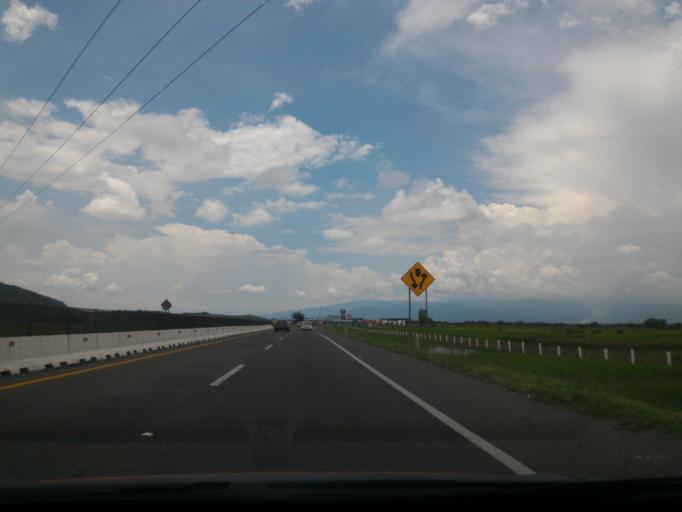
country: MX
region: Jalisco
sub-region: Acatlan de Juarez
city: Villa de los Ninos
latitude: 20.3840
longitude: -103.5764
